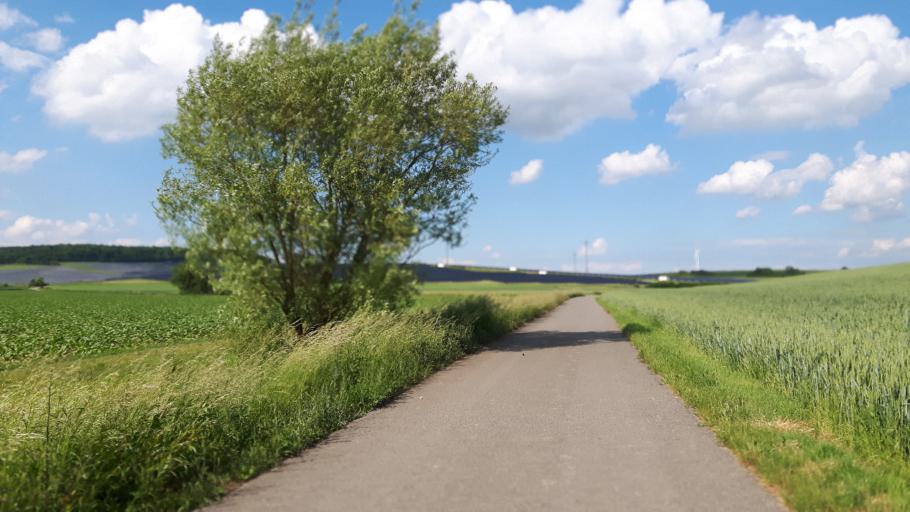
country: DE
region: Bavaria
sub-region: Regierungsbezirk Unterfranken
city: Kirchheim
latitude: 49.6772
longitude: 9.8662
